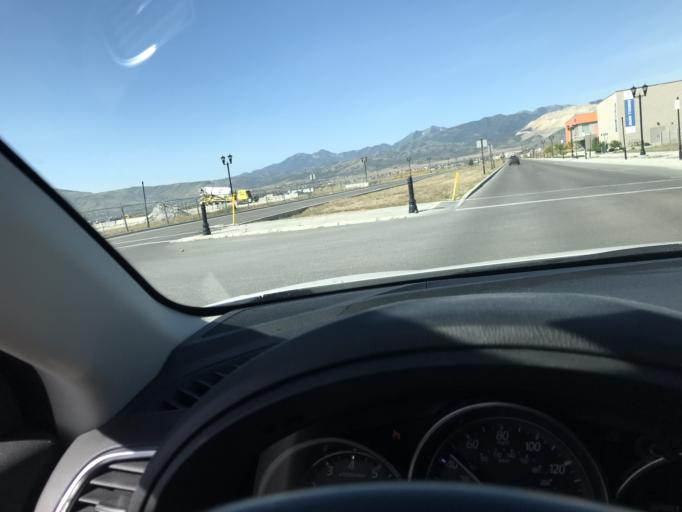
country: US
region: Utah
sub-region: Salt Lake County
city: Herriman
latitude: 40.5575
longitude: -112.0187
